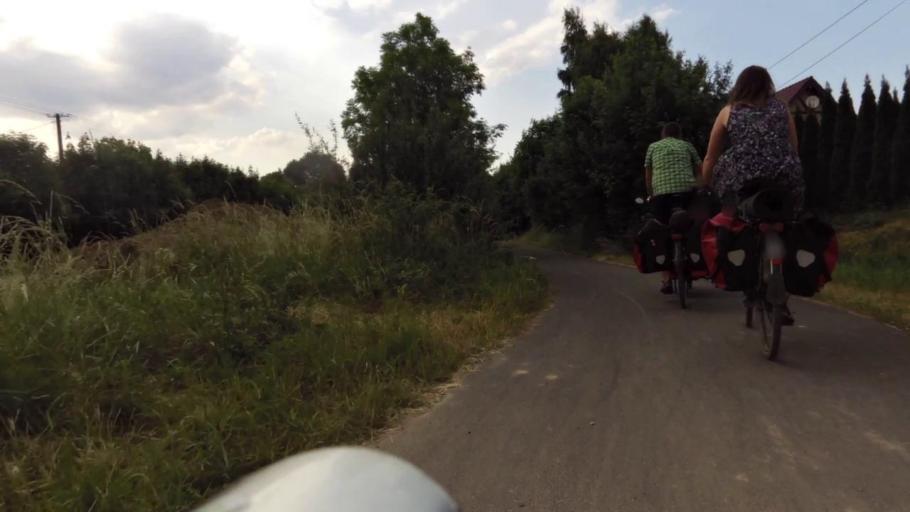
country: PL
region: Kujawsko-Pomorskie
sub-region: Powiat torunski
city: Lubianka
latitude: 53.1327
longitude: 18.4632
